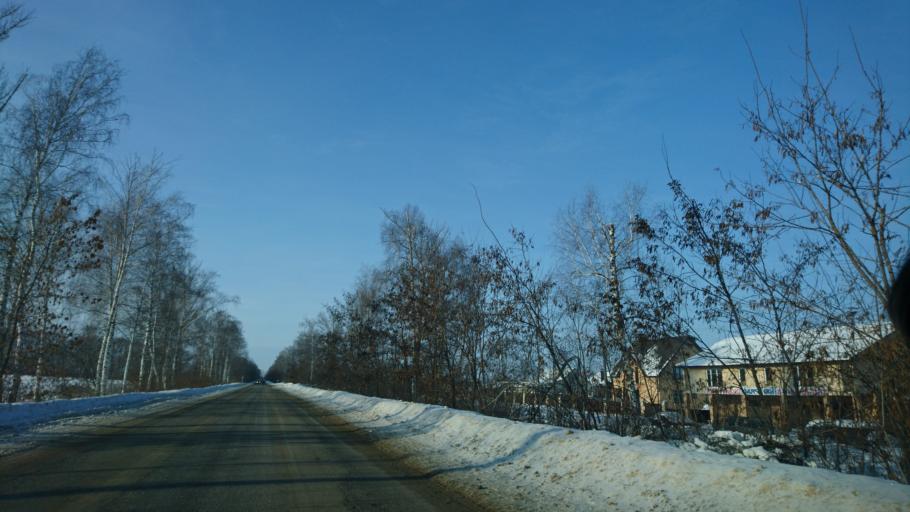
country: RU
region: Belgorod
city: Severnyy
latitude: 50.7266
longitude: 36.5794
